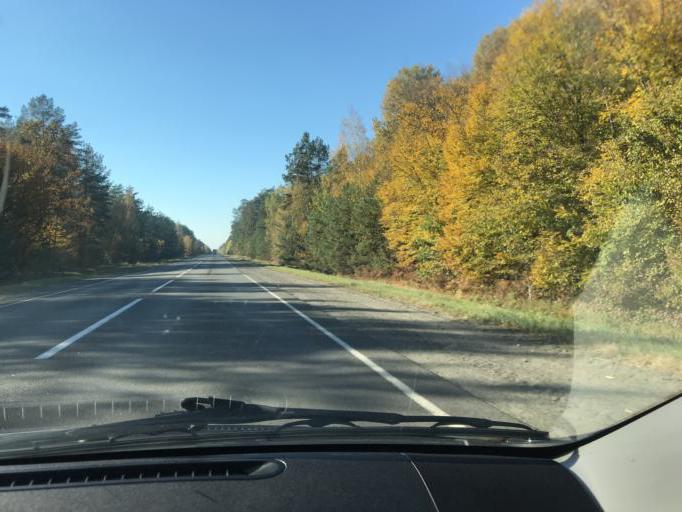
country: BY
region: Brest
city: Mikashevichy
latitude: 52.2421
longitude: 27.3257
